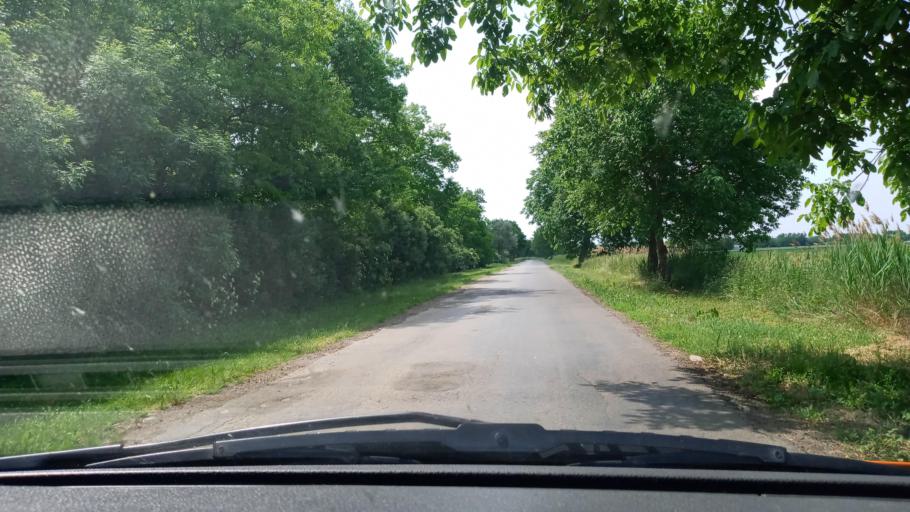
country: HU
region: Baranya
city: Szentlorinc
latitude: 45.9989
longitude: 18.0371
